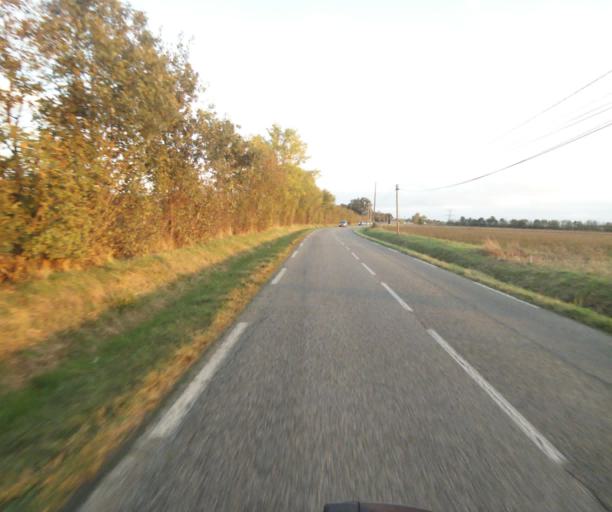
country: FR
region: Midi-Pyrenees
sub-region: Departement du Tarn-et-Garonne
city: Verdun-sur-Garonne
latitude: 43.8314
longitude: 1.2417
